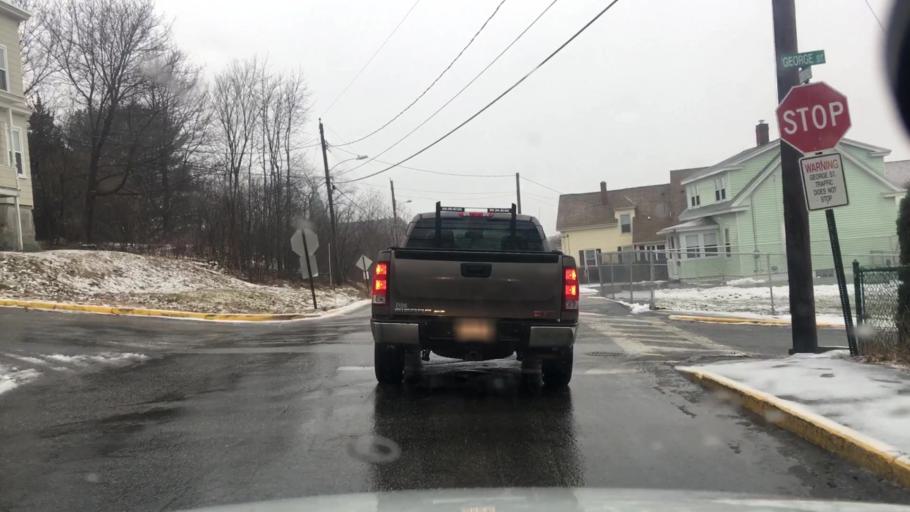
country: US
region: Maine
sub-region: York County
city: Biddeford
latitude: 43.4899
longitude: -70.4459
